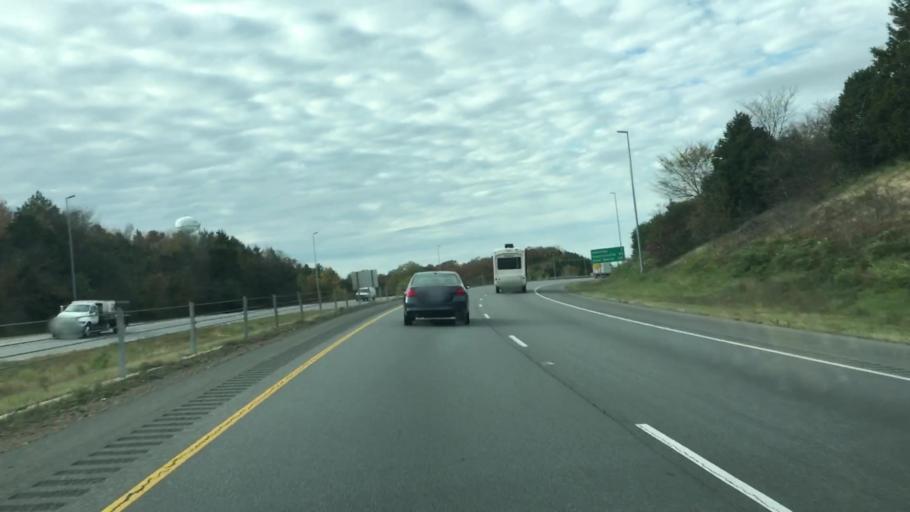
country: US
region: Arkansas
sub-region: Faulkner County
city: Conway
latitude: 35.1140
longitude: -92.4452
